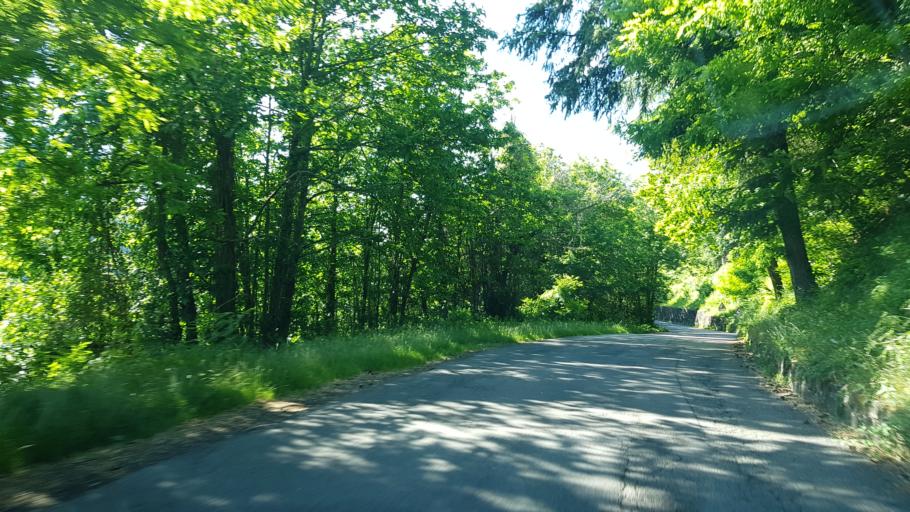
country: IT
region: Tuscany
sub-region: Provincia di Lucca
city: San Romano
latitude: 44.1766
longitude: 10.3403
